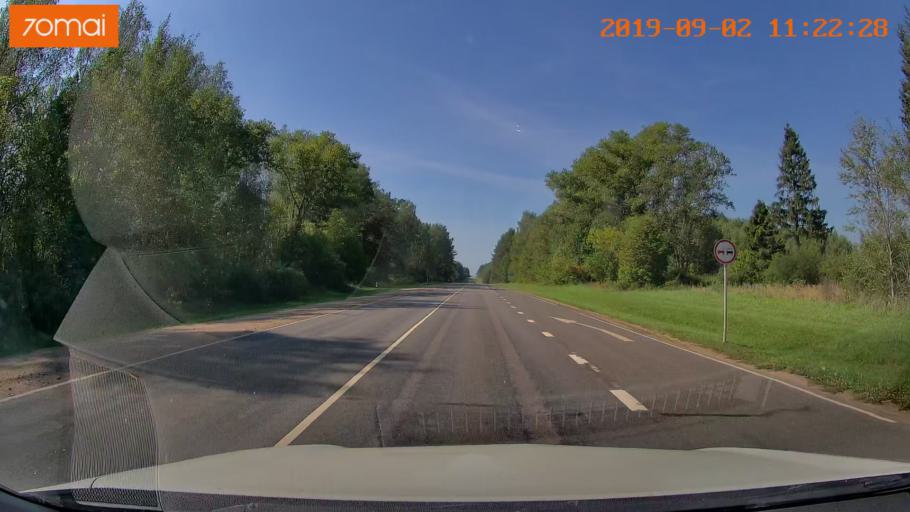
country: RU
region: Smolensk
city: Roslavl'
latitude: 54.0255
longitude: 33.0126
